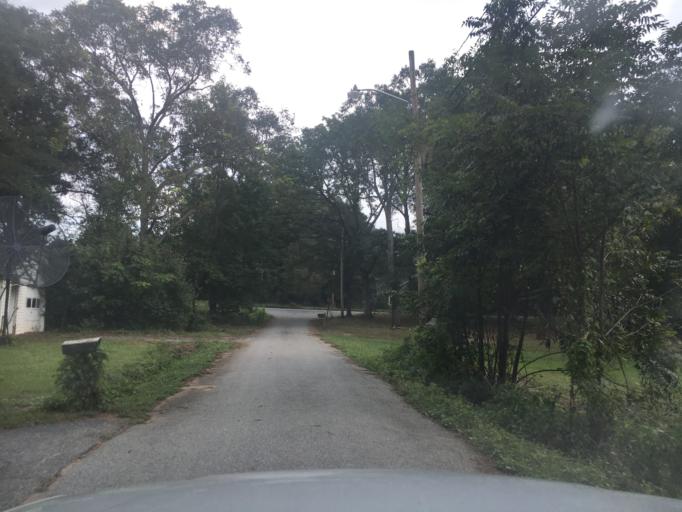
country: US
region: South Carolina
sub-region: Spartanburg County
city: Duncan
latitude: 34.9352
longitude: -82.1381
